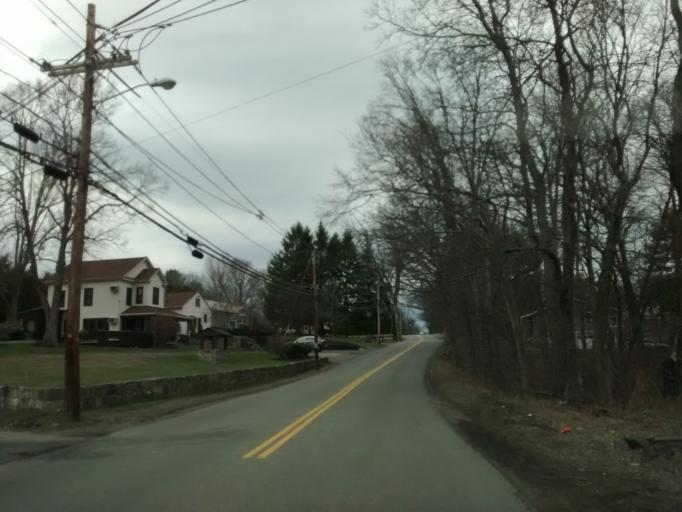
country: US
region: Massachusetts
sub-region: Worcester County
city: Grafton
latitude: 42.1858
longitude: -71.7037
